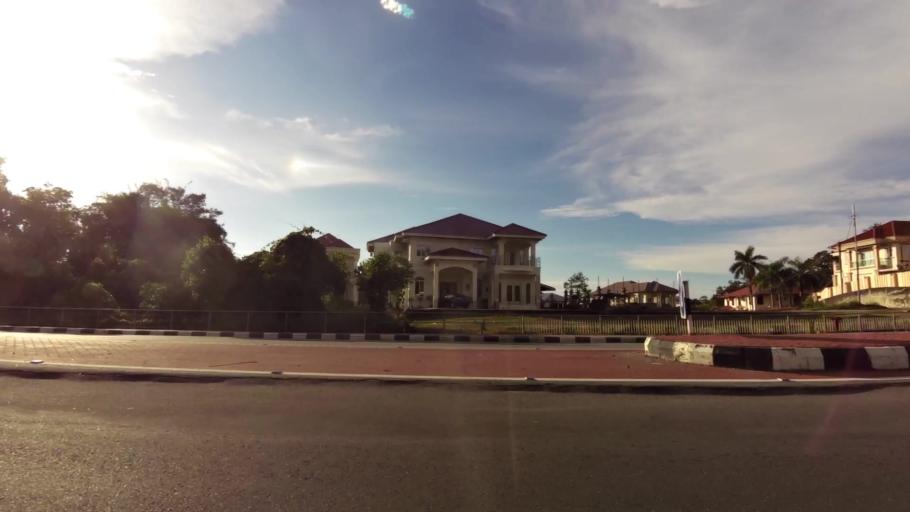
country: BN
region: Brunei and Muara
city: Bandar Seri Begawan
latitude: 4.9735
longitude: 114.9826
